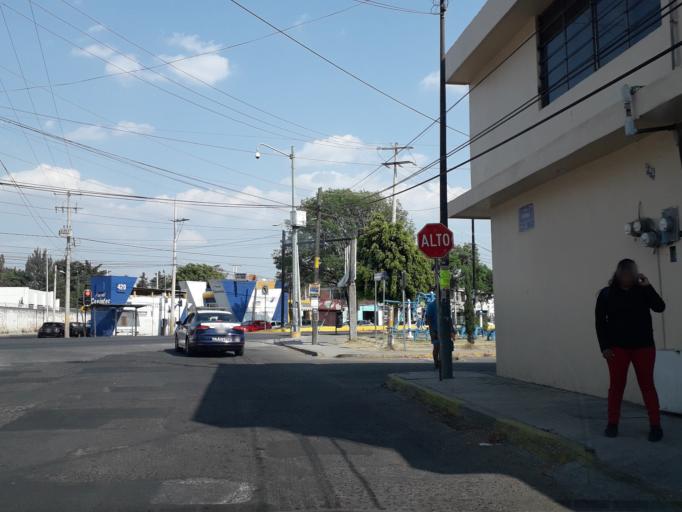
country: MX
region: Puebla
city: Puebla
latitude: 19.0153
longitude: -98.2102
